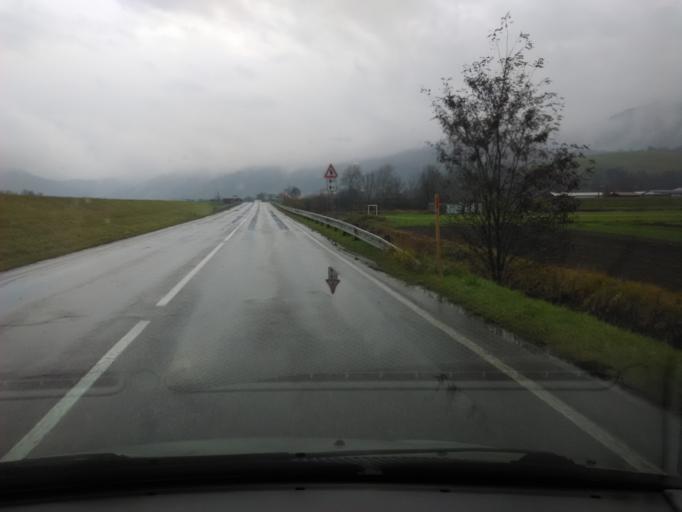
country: SK
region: Trenciansky
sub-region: Okres Povazska Bystrica
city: Povazska Bystrica
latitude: 49.1668
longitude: 18.4726
